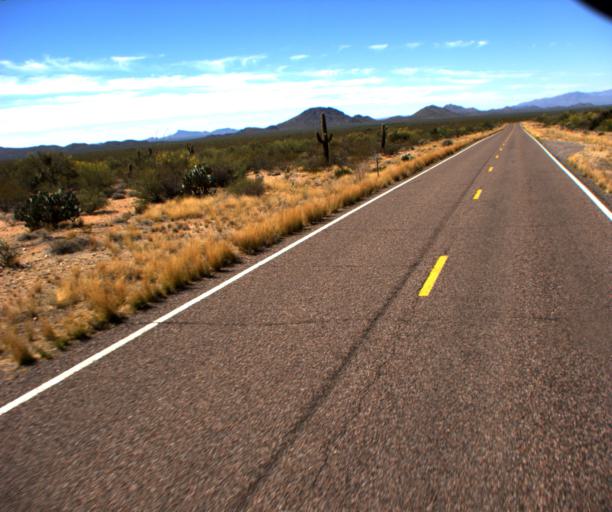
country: US
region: Arizona
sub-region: Yavapai County
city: Congress
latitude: 34.1010
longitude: -112.9975
